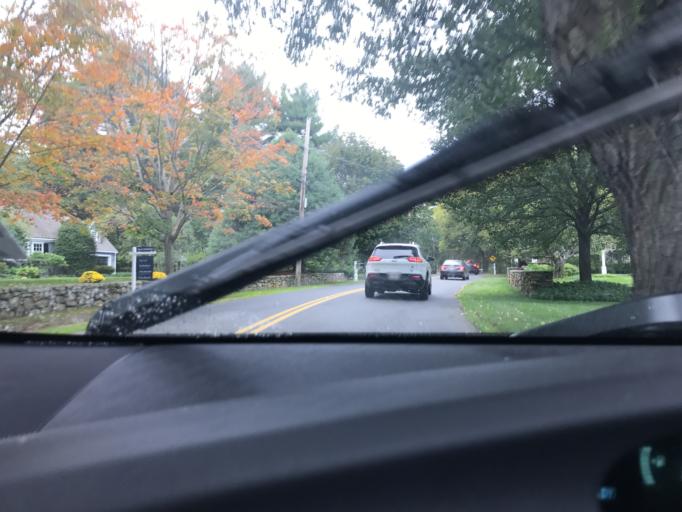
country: US
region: Massachusetts
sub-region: Middlesex County
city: Concord
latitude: 42.4735
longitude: -71.3620
